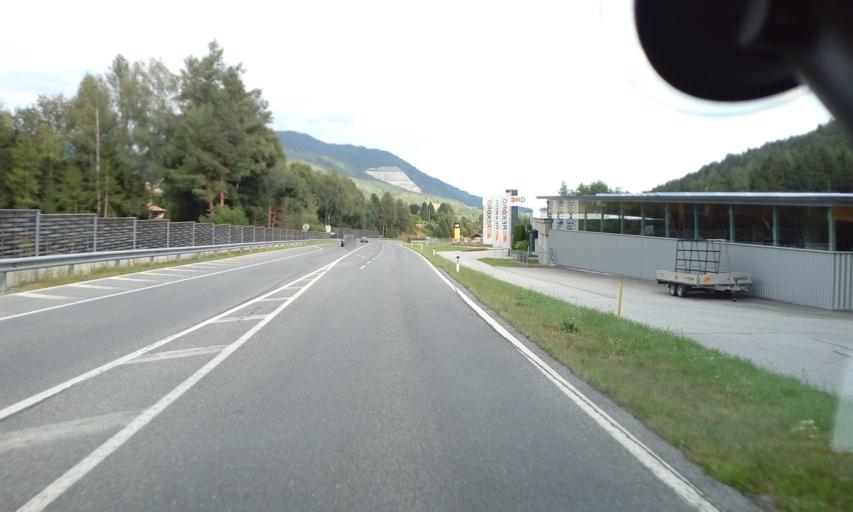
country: AT
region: Carinthia
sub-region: Politischer Bezirk Villach Land
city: Fresach
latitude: 46.6618
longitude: 13.7407
